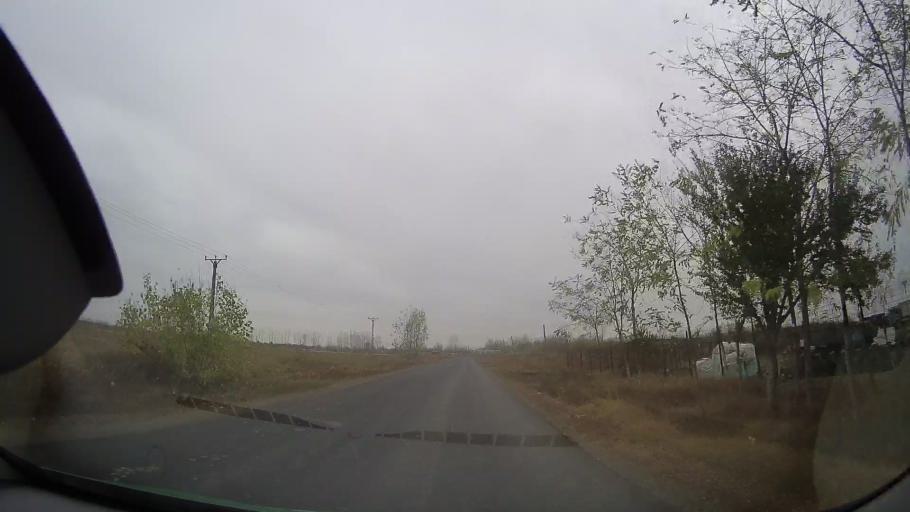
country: RO
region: Braila
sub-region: Comuna Ciocile
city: Ciocile
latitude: 44.8175
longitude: 27.2577
